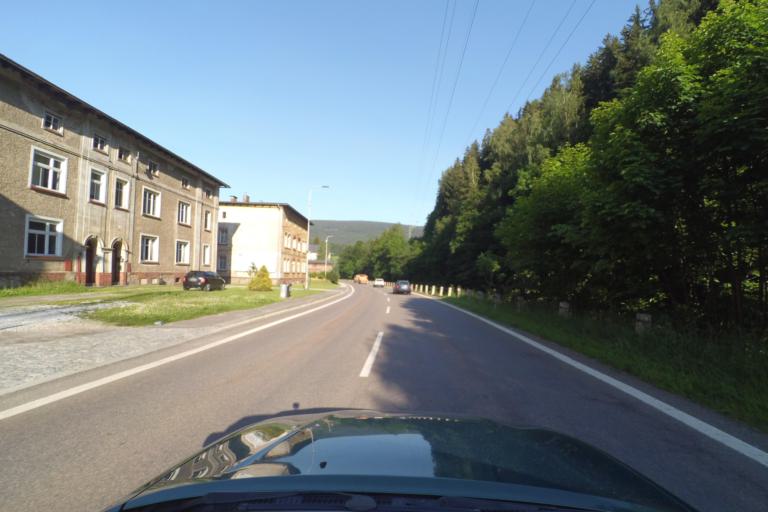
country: CZ
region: Kralovehradecky
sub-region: Okres Trutnov
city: Svoboda nad Upou
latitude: 50.6627
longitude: 15.8116
